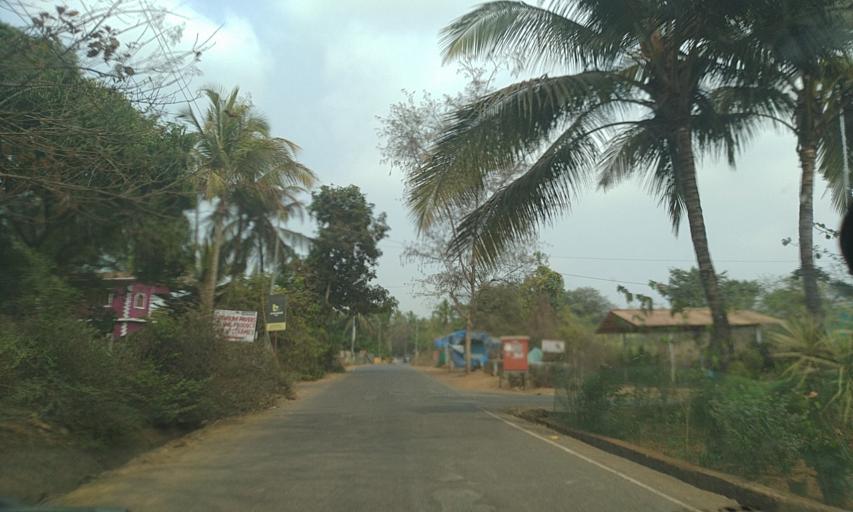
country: IN
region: Goa
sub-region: South Goa
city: Raia
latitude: 15.3072
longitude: 73.9521
